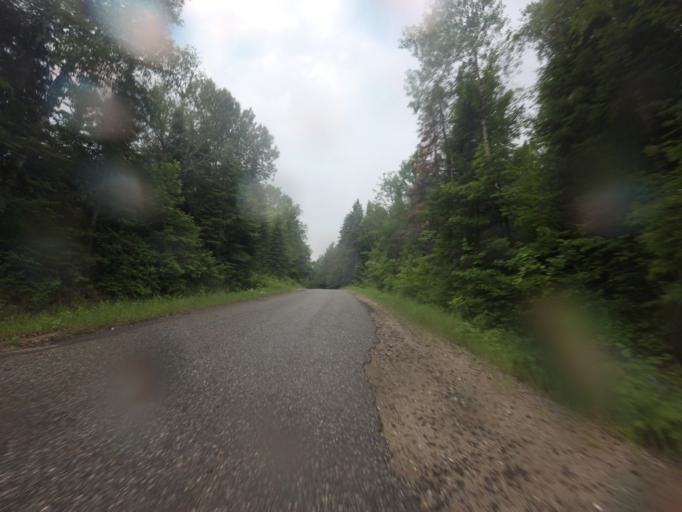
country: CA
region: Quebec
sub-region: Outaouais
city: Maniwaki
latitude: 46.4323
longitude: -75.9467
